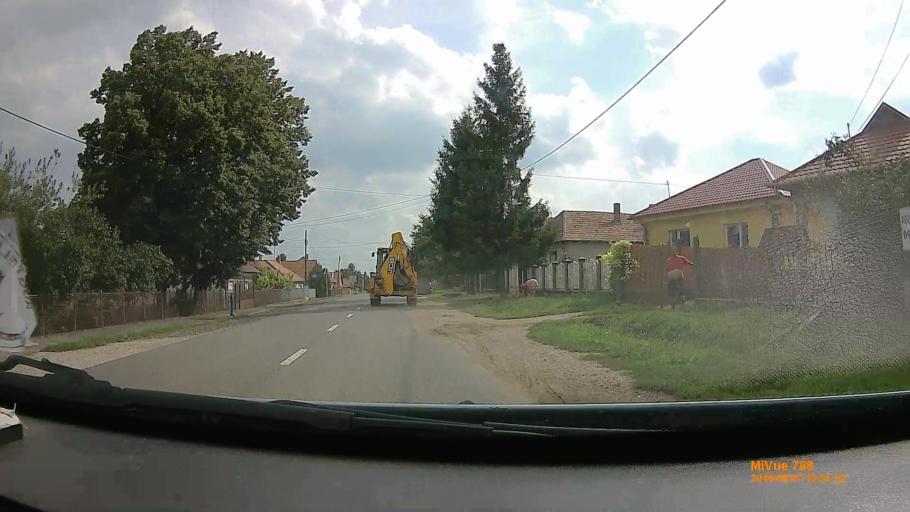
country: HU
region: Borsod-Abauj-Zemplen
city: Encs
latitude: 48.4164
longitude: 21.1740
